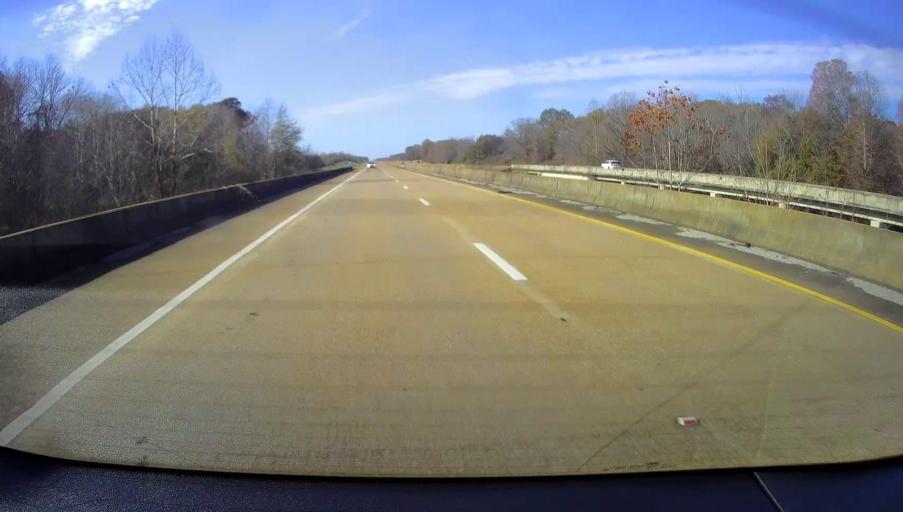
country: US
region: Mississippi
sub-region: Benton County
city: Ashland
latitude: 34.9460
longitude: -89.1959
